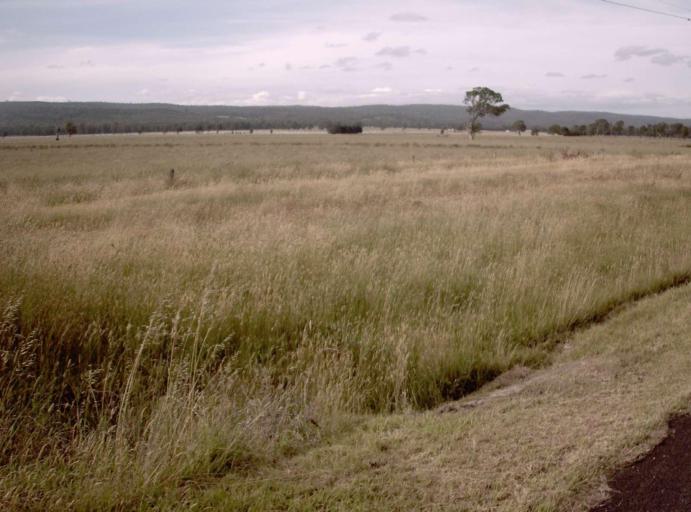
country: AU
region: Victoria
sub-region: Latrobe
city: Traralgon
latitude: -38.0886
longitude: 146.6027
